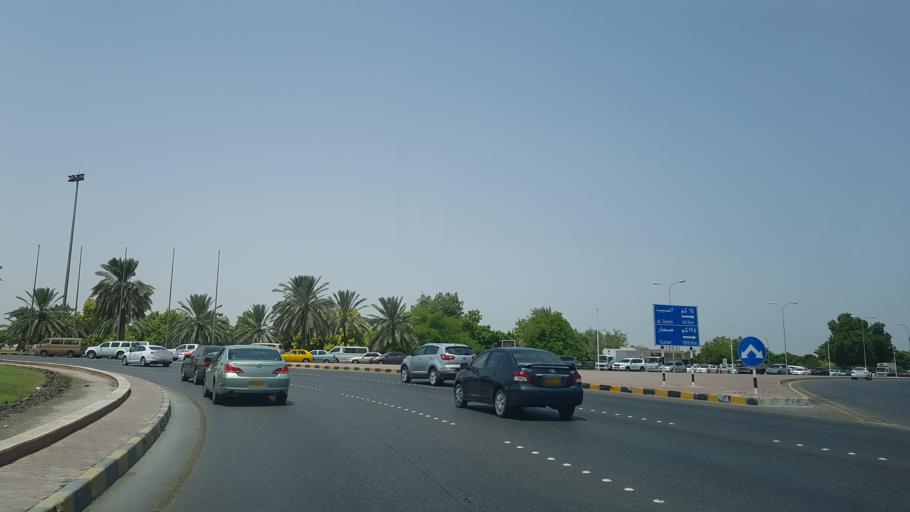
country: OM
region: Muhafazat Masqat
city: As Sib al Jadidah
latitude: 23.5876
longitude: 58.2523
